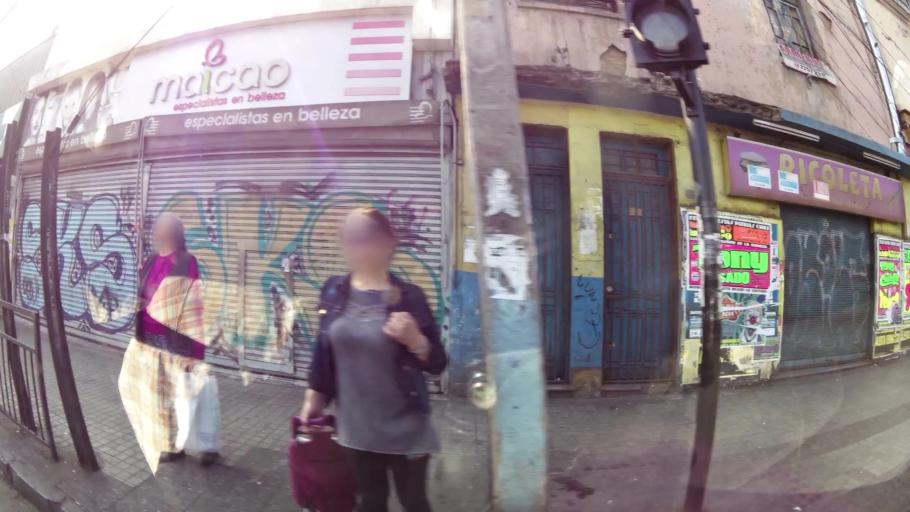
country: CL
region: Santiago Metropolitan
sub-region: Provincia de Santiago
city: Santiago
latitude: -33.4059
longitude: -70.6431
